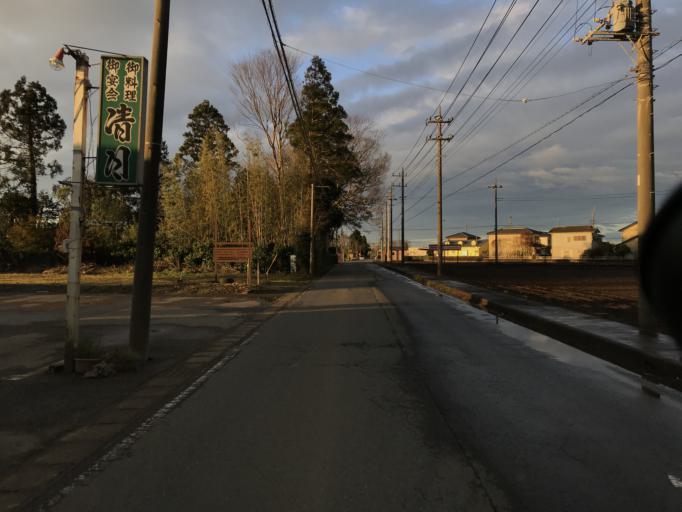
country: JP
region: Chiba
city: Sawara
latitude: 35.8259
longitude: 140.4580
